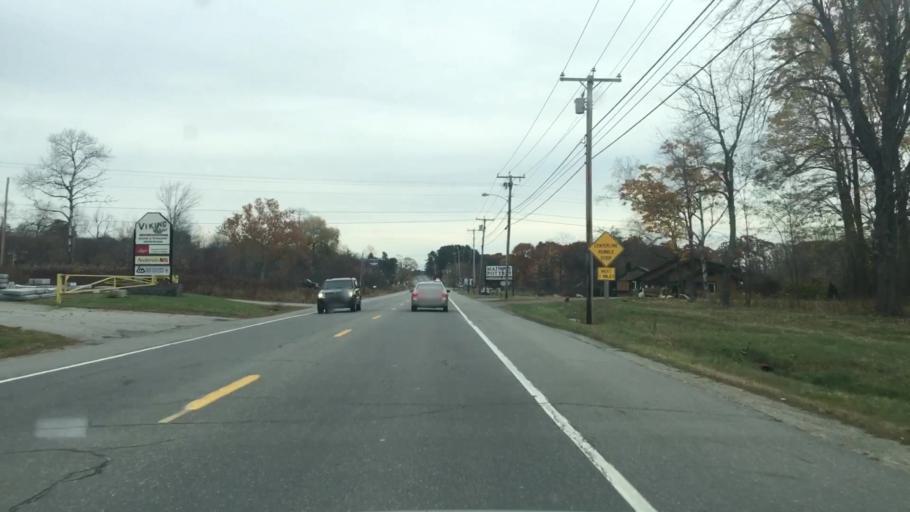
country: US
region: Maine
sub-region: Waldo County
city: Belfast
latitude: 44.4294
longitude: -68.9752
